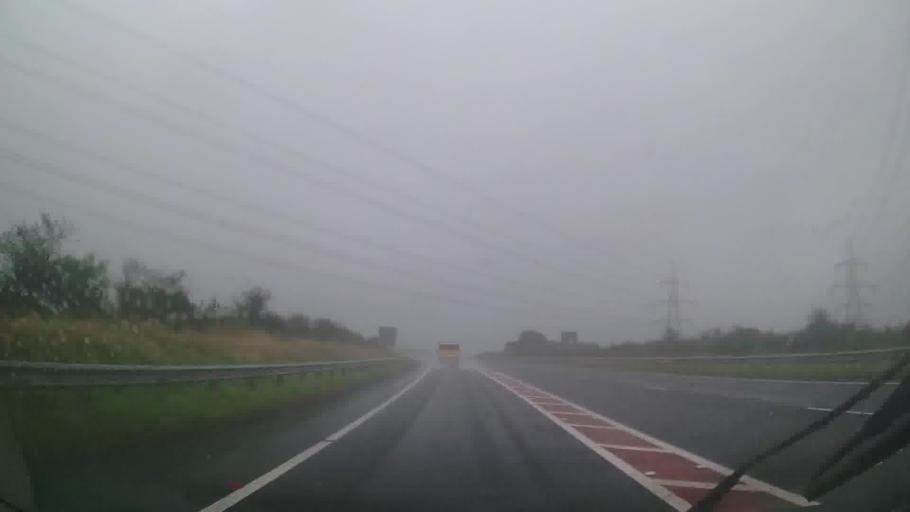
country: GB
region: Wales
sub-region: Carmarthenshire
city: Whitland
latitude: 51.7853
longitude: -4.6033
